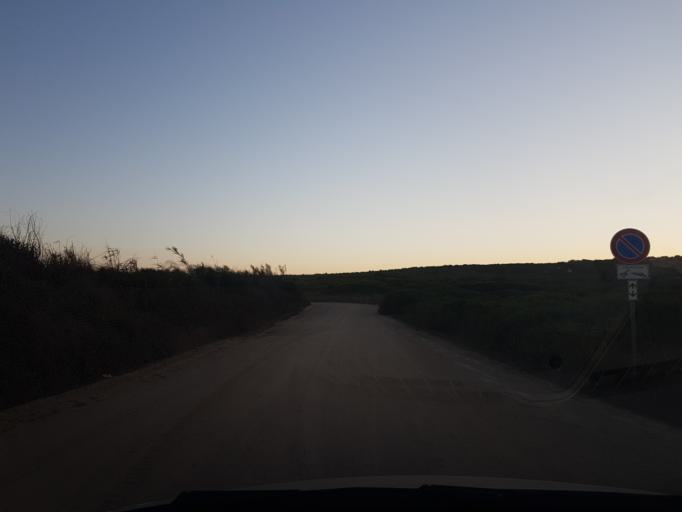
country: IT
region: Sardinia
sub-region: Provincia di Oristano
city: Riola Sardo
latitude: 40.0418
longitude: 8.3972
